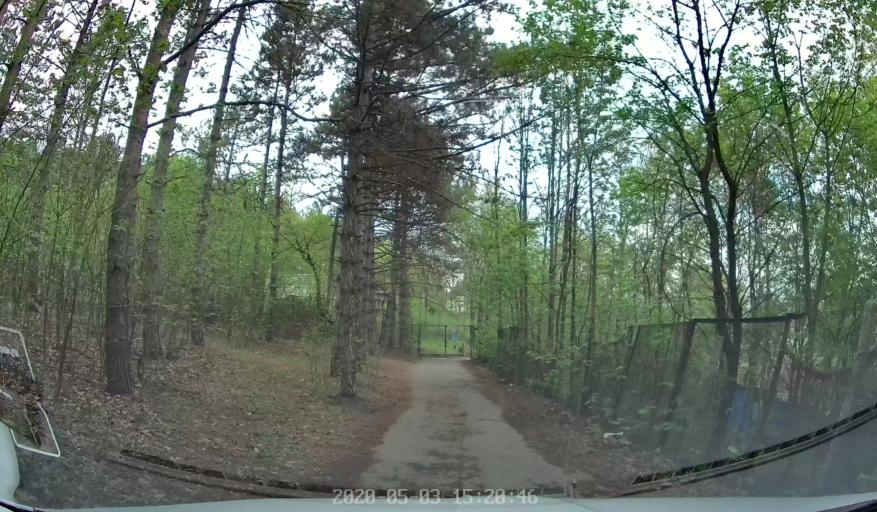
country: MD
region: Chisinau
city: Vatra
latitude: 47.0871
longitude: 28.7125
